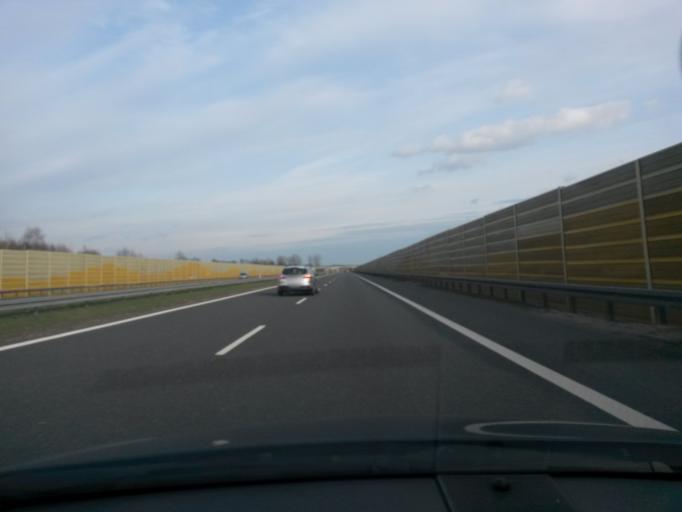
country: PL
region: Lodz Voivodeship
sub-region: Powiat leczycki
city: Swinice Warckie
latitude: 52.0301
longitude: 18.8963
